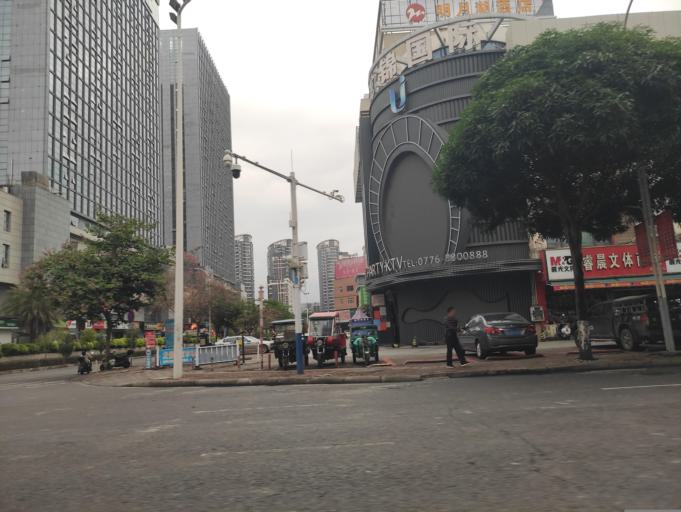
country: CN
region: Guangxi Zhuangzu Zizhiqu
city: Baise City
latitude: 23.8912
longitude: 106.6302
